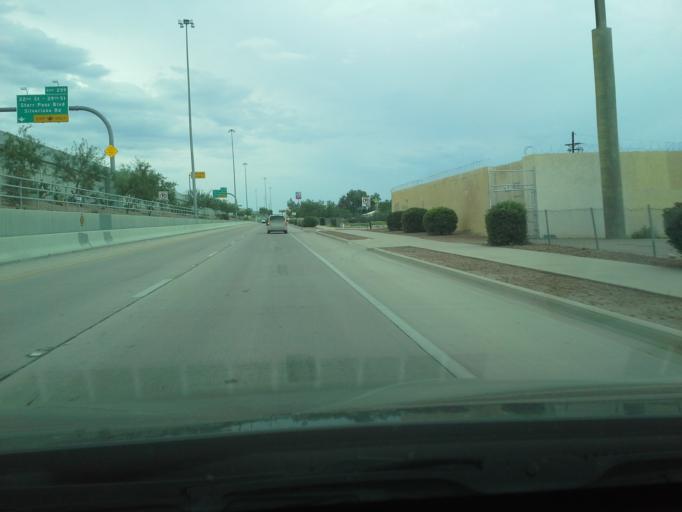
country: US
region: Arizona
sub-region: Pima County
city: South Tucson
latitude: 32.2149
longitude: -110.9802
